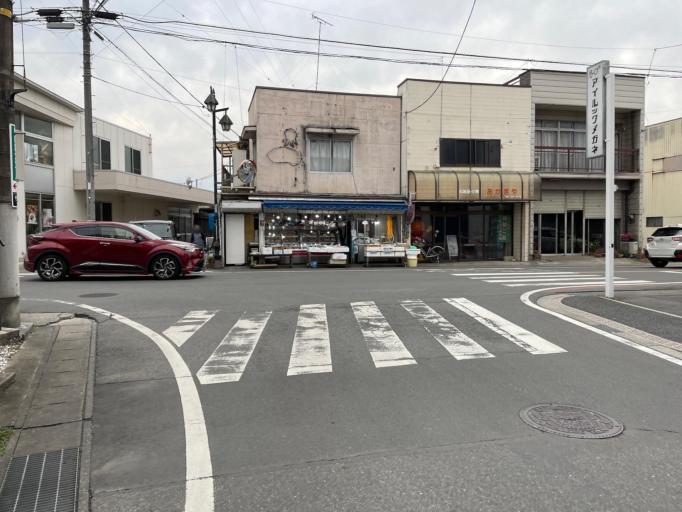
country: JP
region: Gunma
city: Fujioka
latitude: 36.2484
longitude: 139.0815
